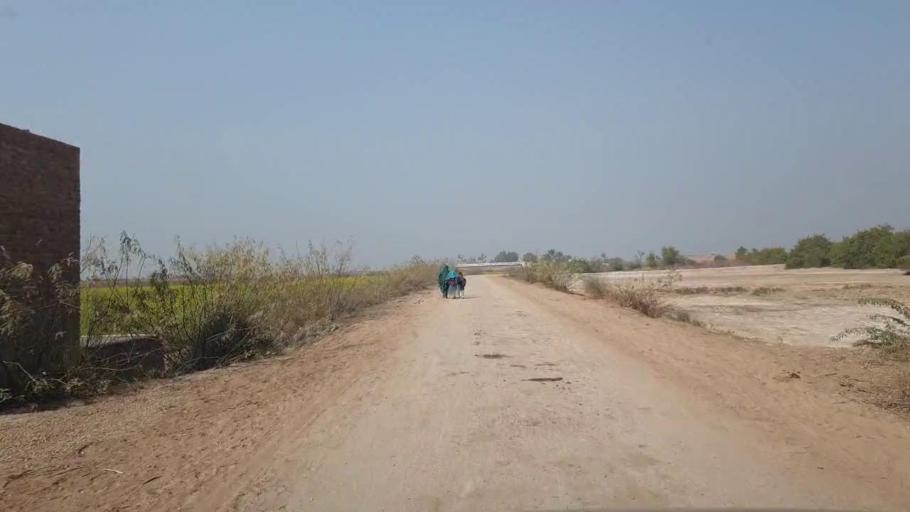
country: PK
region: Sindh
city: Hala
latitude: 25.9506
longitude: 68.4654
